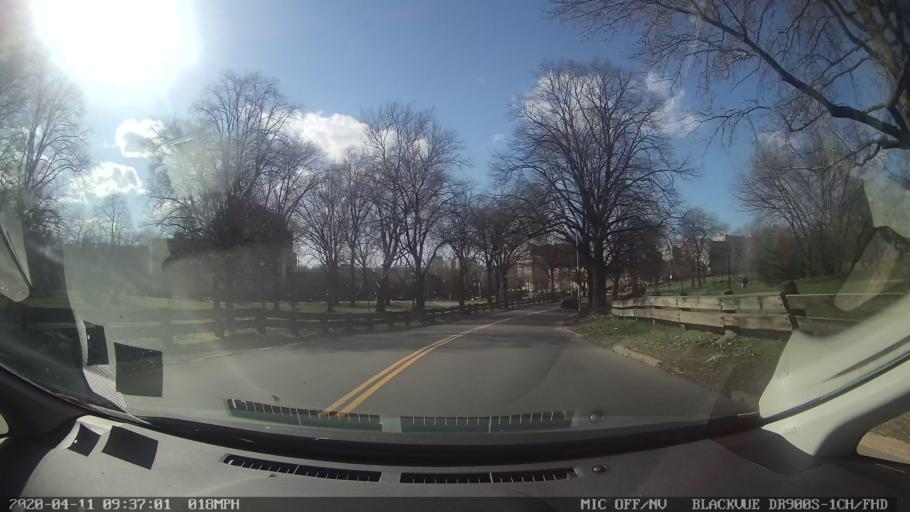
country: US
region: New York
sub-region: Bronx
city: The Bronx
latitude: 40.8366
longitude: -73.8989
